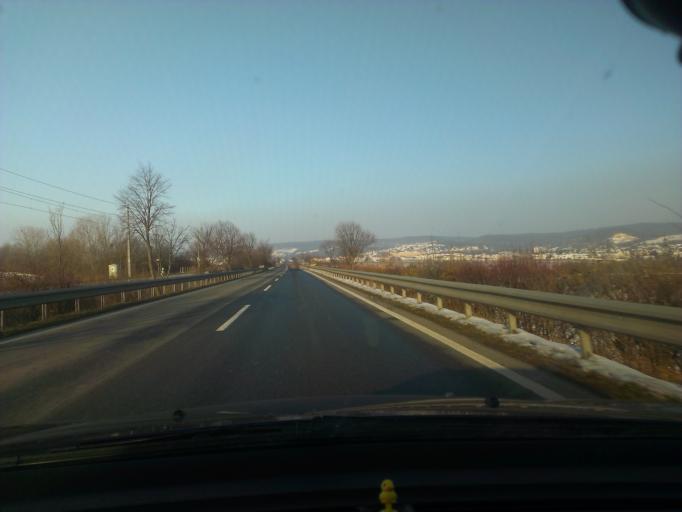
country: AT
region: Burgenland
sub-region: Eisenstadt-Umgebung
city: Trausdorf an der Wulka
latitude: 47.8440
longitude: 16.5601
